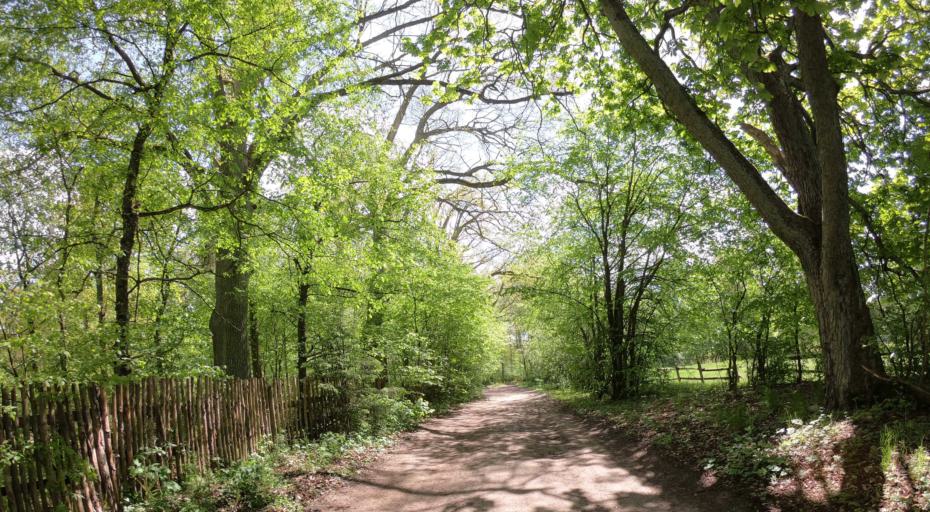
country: PL
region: West Pomeranian Voivodeship
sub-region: Powiat lobeski
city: Lobez
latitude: 53.6010
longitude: 15.6531
